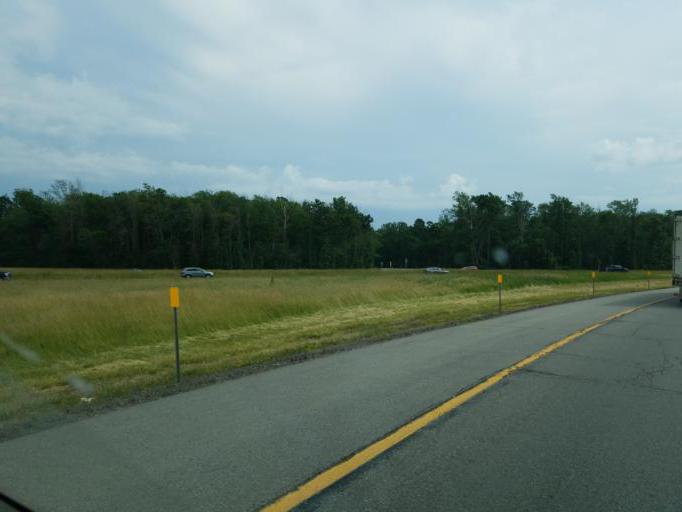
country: US
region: New York
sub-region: Erie County
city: Hamburg
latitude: 42.7444
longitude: -78.8412
